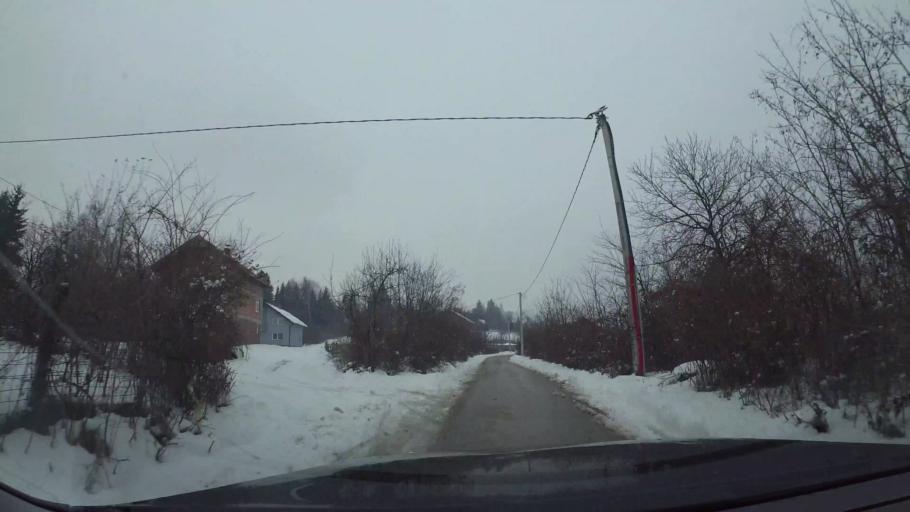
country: BA
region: Federation of Bosnia and Herzegovina
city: Hadzici
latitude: 43.8501
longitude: 18.2695
